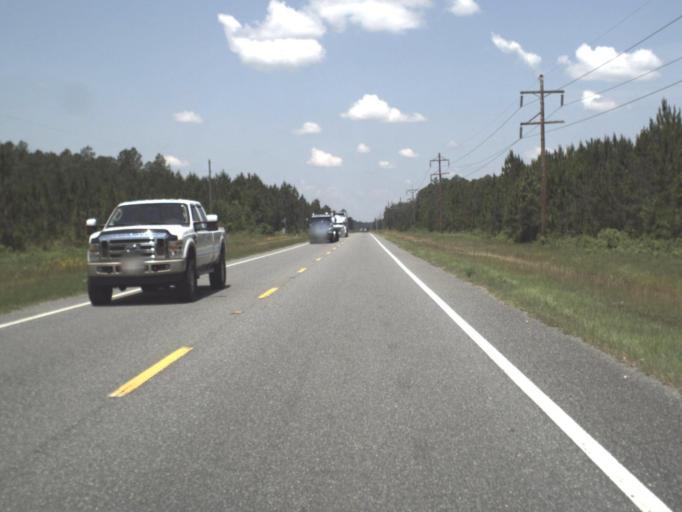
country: US
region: Florida
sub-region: Bradford County
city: Starke
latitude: 29.9765
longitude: -82.2255
